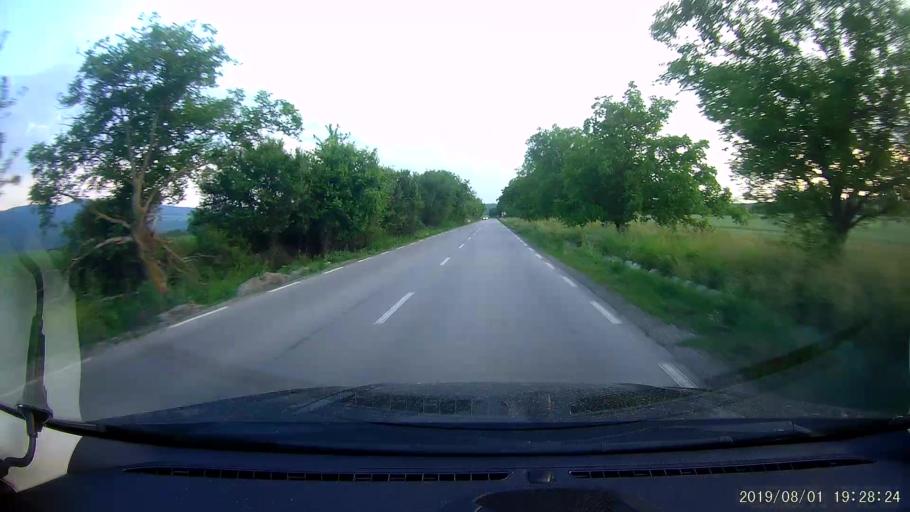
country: BG
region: Burgas
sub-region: Obshtina Sungurlare
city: Sungurlare
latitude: 42.8428
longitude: 26.9179
